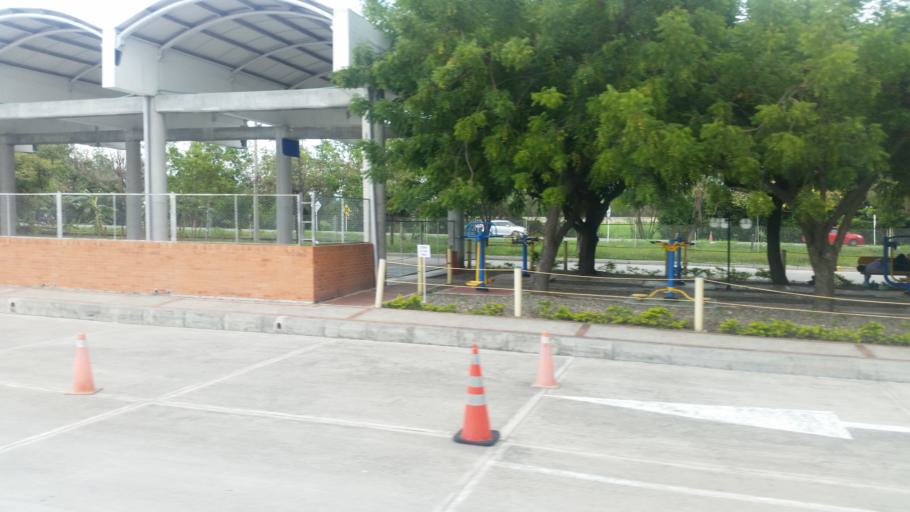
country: CO
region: Tolima
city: Espinal
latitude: 4.1647
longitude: -74.8829
